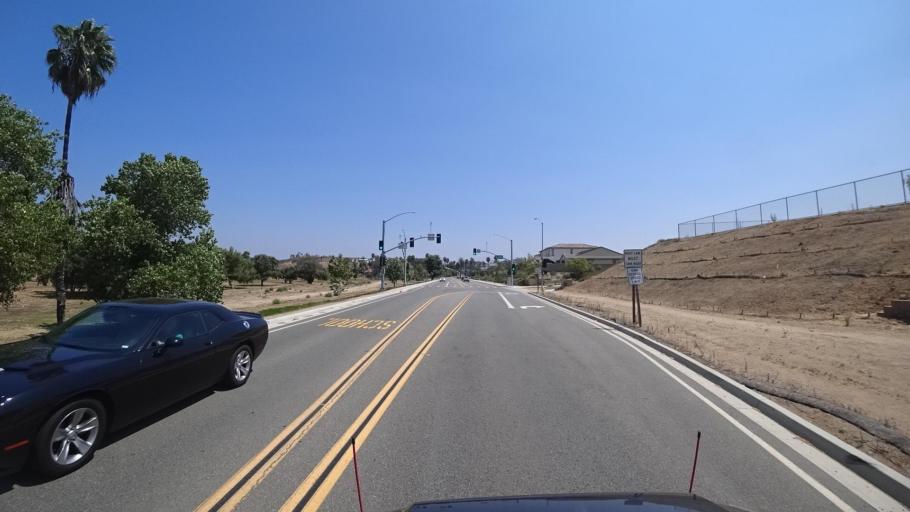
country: US
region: California
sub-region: San Diego County
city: Bonsall
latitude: 33.2888
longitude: -117.2197
